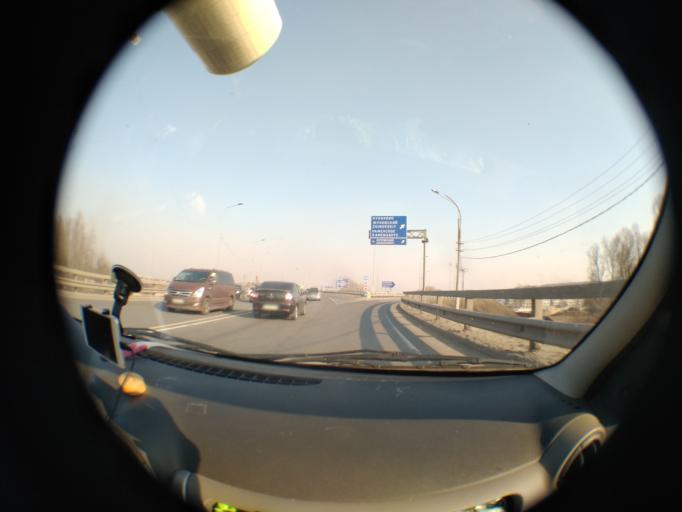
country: RU
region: Moskovskaya
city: Ostrovtsy
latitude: 55.5683
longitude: 38.0369
